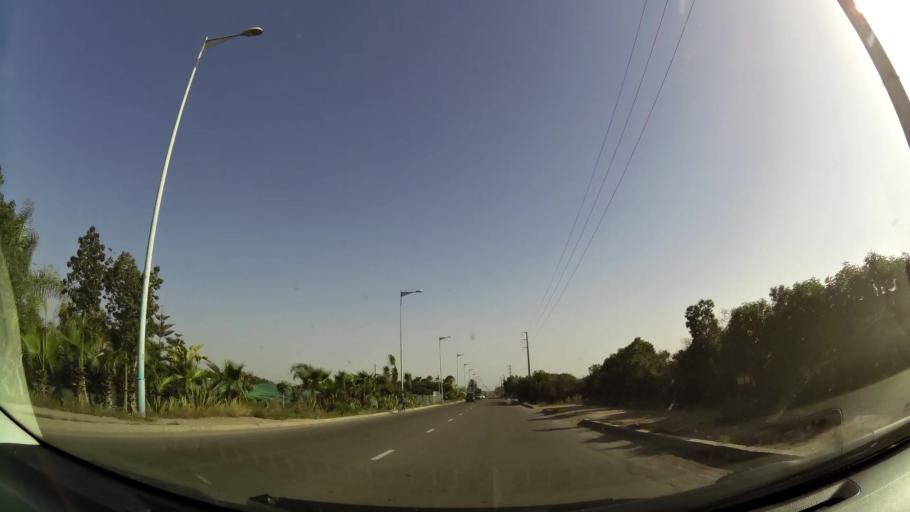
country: MA
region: Souss-Massa-Draa
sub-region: Inezgane-Ait Mellou
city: Inezgane
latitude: 30.3674
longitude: -9.5061
